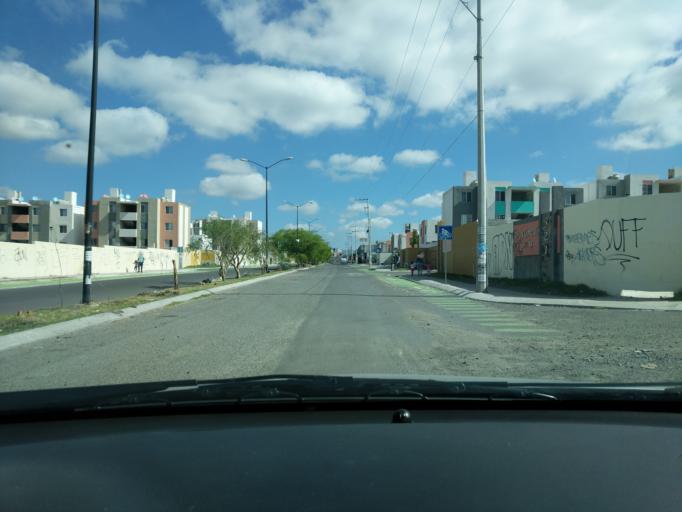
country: MX
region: Queretaro
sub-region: Queretaro
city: Patria Nueva
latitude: 20.6377
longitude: -100.4795
